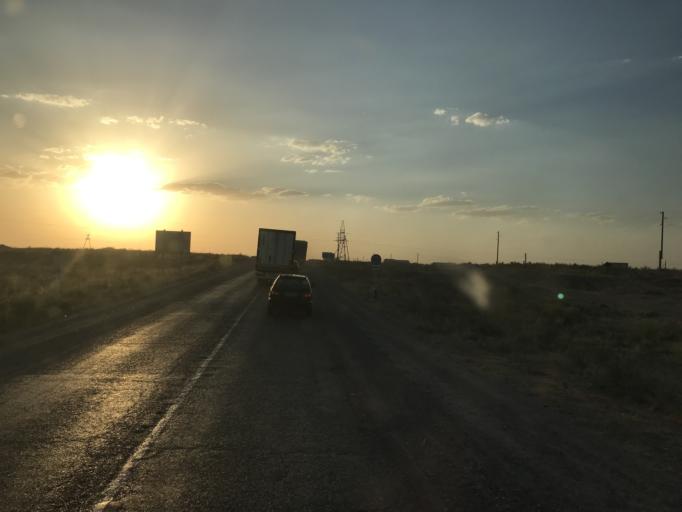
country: UZ
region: Toshkent
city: Yangiyul
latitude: 41.3285
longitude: 68.8924
